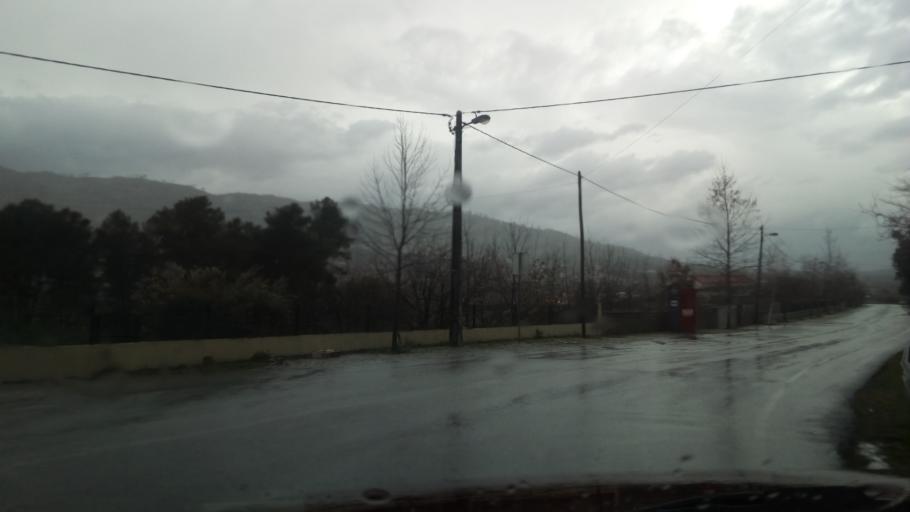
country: PT
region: Guarda
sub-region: Guarda
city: Guarda
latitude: 40.5987
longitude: -7.2909
